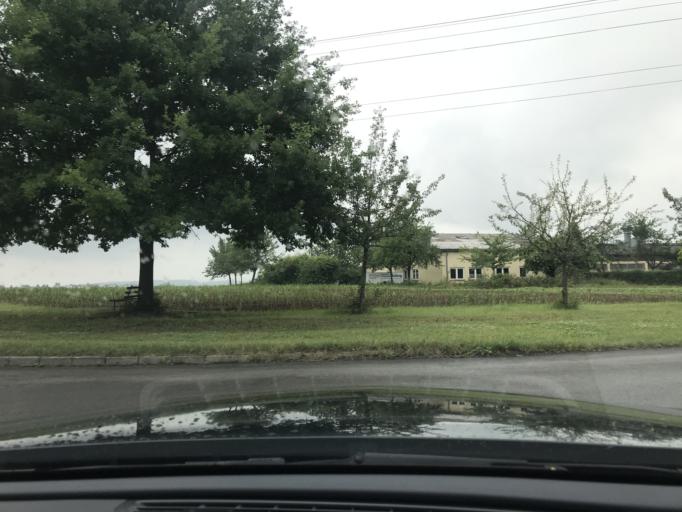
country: DE
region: Baden-Wuerttemberg
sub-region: Regierungsbezirk Stuttgart
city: Waiblingen
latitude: 48.8454
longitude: 9.3033
